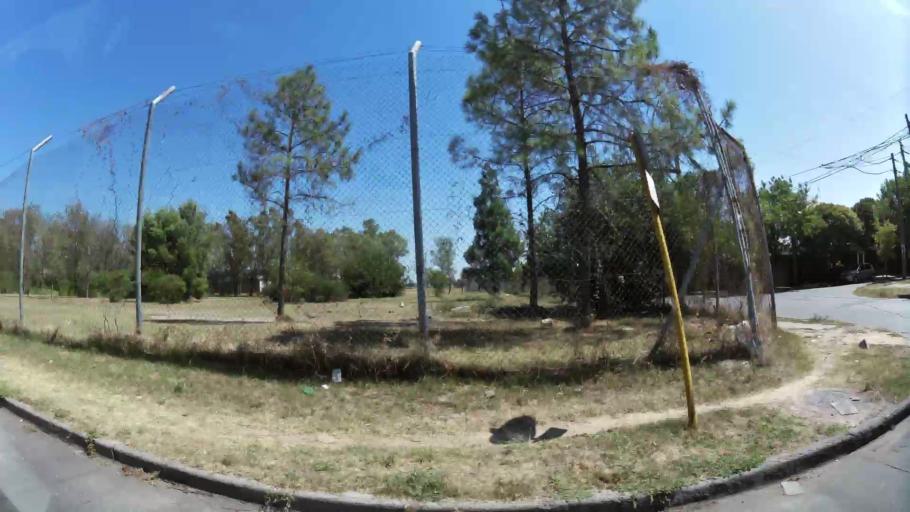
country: AR
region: Cordoba
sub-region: Departamento de Capital
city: Cordoba
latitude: -31.4542
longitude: -64.1629
